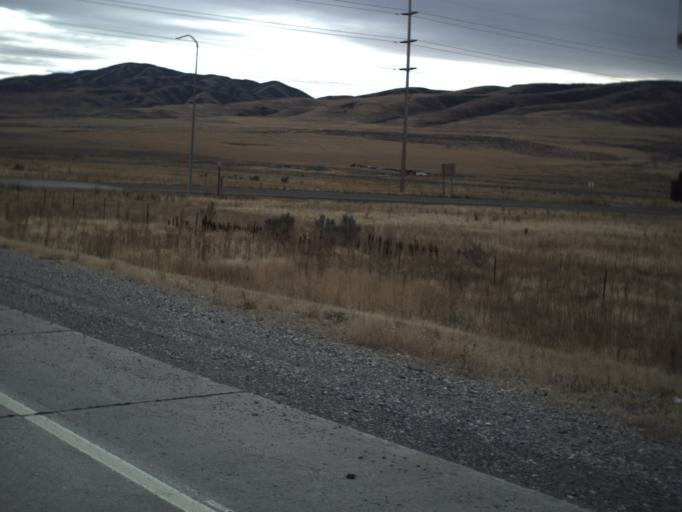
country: US
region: Utah
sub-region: Box Elder County
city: Garland
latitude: 41.8874
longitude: -112.1717
